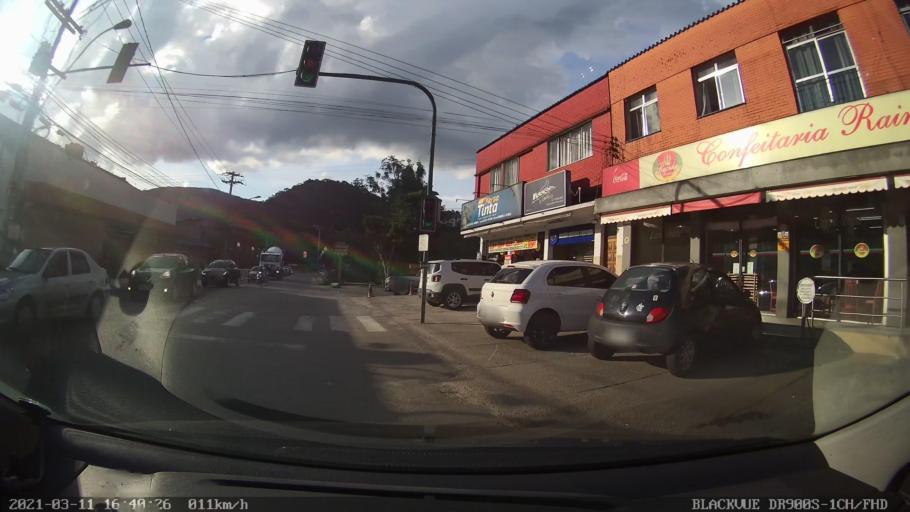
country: BR
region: Rio de Janeiro
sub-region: Petropolis
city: Petropolis
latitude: -22.4153
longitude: -43.1394
